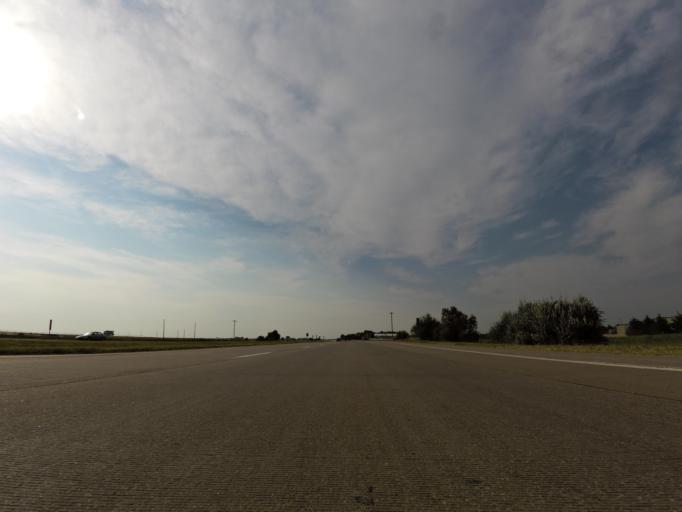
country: US
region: Kansas
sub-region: Sedgwick County
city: Colwich
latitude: 37.8384
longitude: -97.5712
